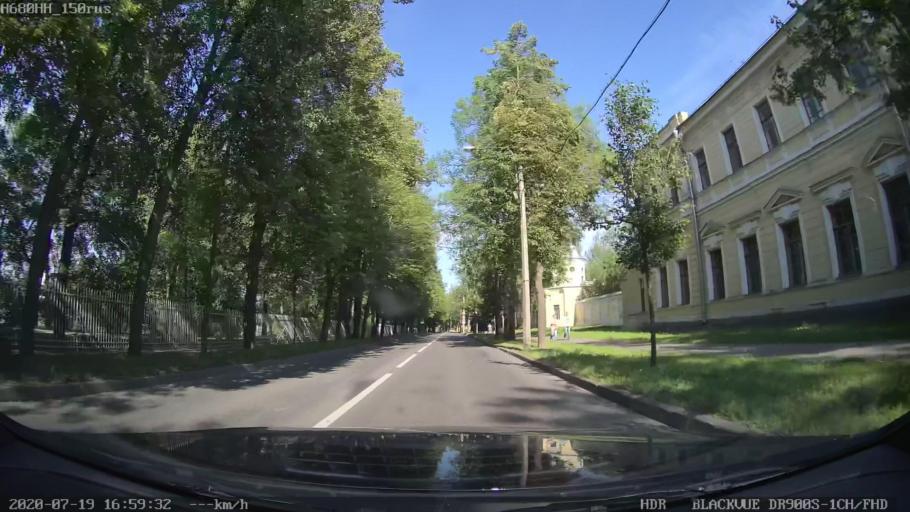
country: RU
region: St.-Petersburg
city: Pushkin
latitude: 59.7091
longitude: 30.3931
